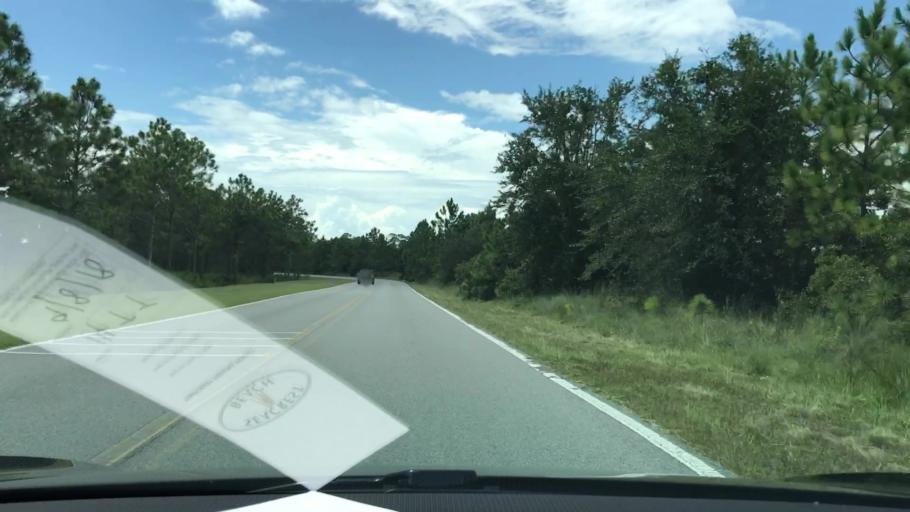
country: US
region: Florida
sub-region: Walton County
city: Seaside
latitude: 30.2925
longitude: -86.0351
